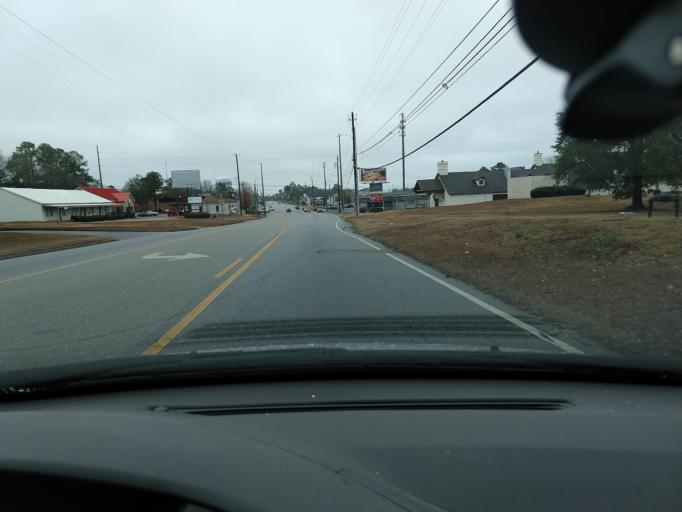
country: US
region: Alabama
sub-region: Houston County
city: Dothan
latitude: 31.2266
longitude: -85.4345
